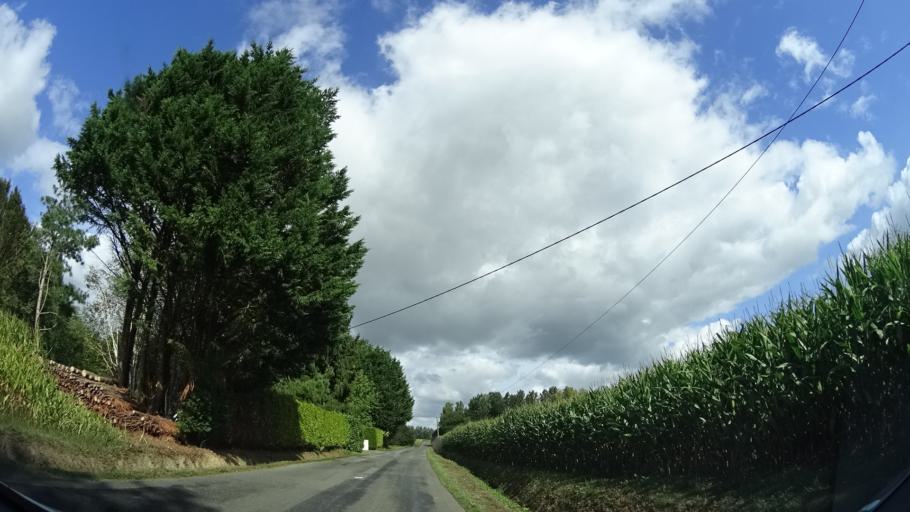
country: FR
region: Brittany
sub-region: Departement d'Ille-et-Vilaine
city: Dinge
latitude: 48.3356
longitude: -1.6908
